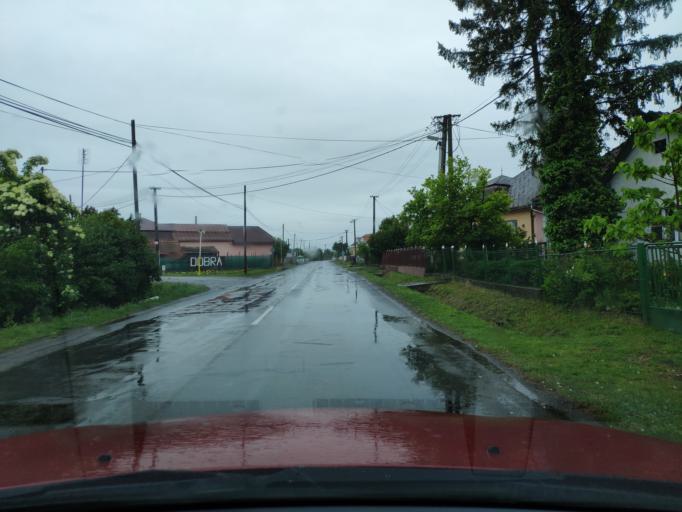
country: SK
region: Kosicky
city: Cierna nad Tisou
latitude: 48.4149
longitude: 22.0279
